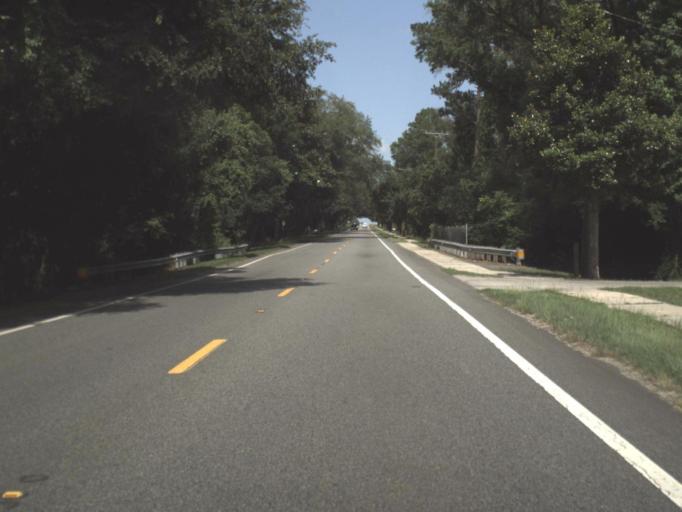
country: US
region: Florida
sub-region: Clay County
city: Asbury Lake
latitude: 29.9827
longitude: -81.7921
